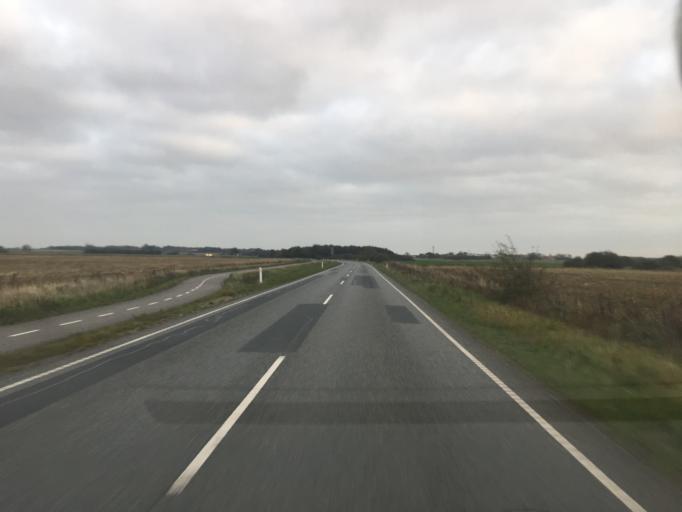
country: DE
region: Schleswig-Holstein
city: Aventoft
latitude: 54.9565
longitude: 8.7677
